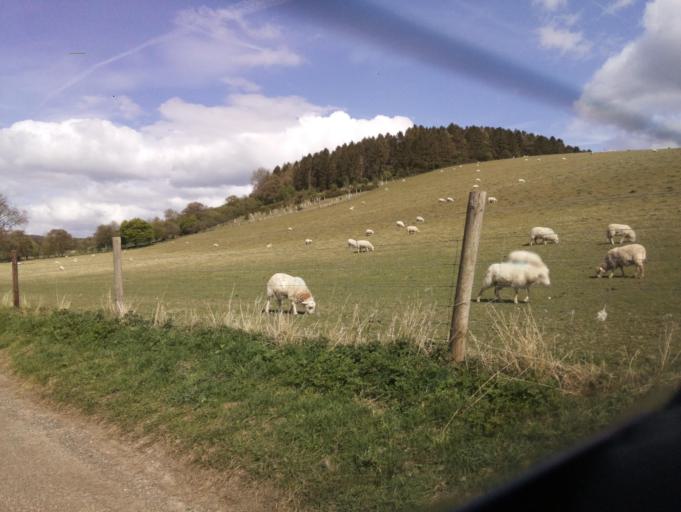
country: GB
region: England
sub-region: West Berkshire
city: Kintbury
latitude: 51.3356
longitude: -1.4698
